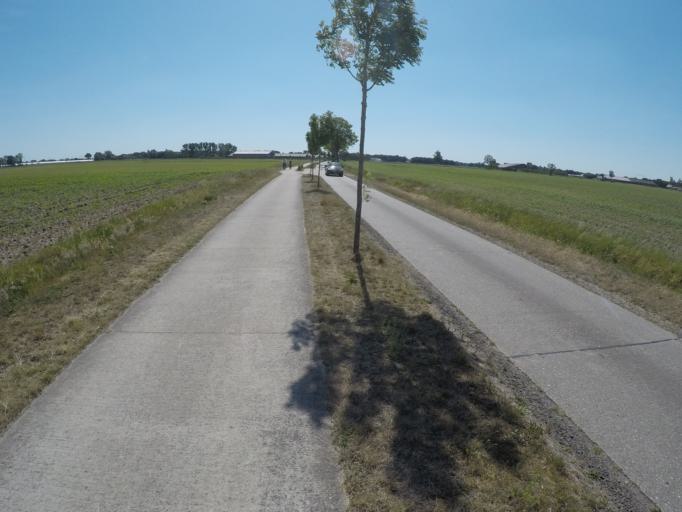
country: BE
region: Flanders
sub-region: Provincie Antwerpen
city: Wuustwezel
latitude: 51.4230
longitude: 4.5790
